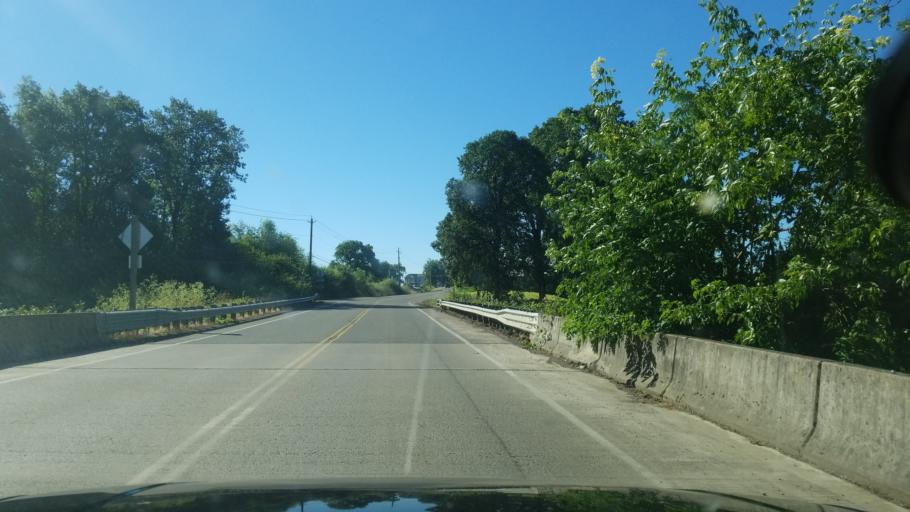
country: US
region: Oregon
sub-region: Yamhill County
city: McMinnville
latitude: 45.2297
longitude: -123.2316
